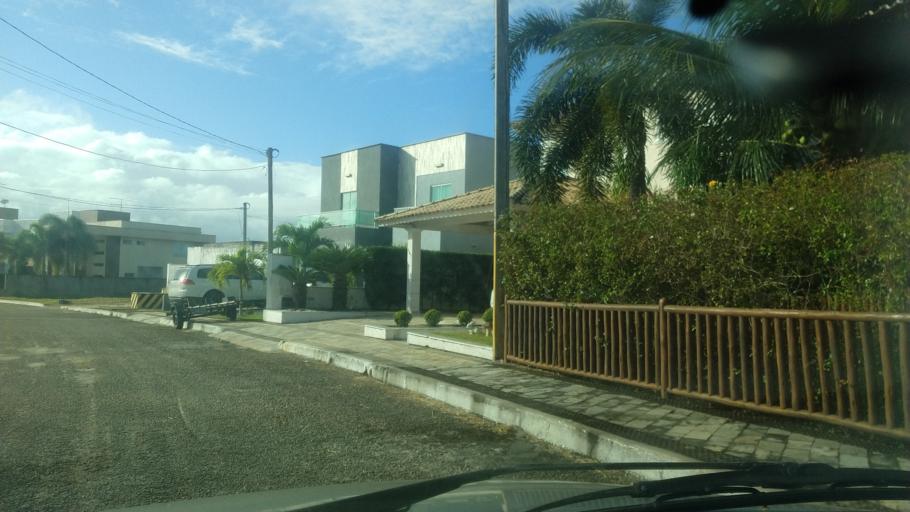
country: BR
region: Rio Grande do Norte
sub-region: Parnamirim
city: Parnamirim
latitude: -5.9260
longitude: -35.2199
